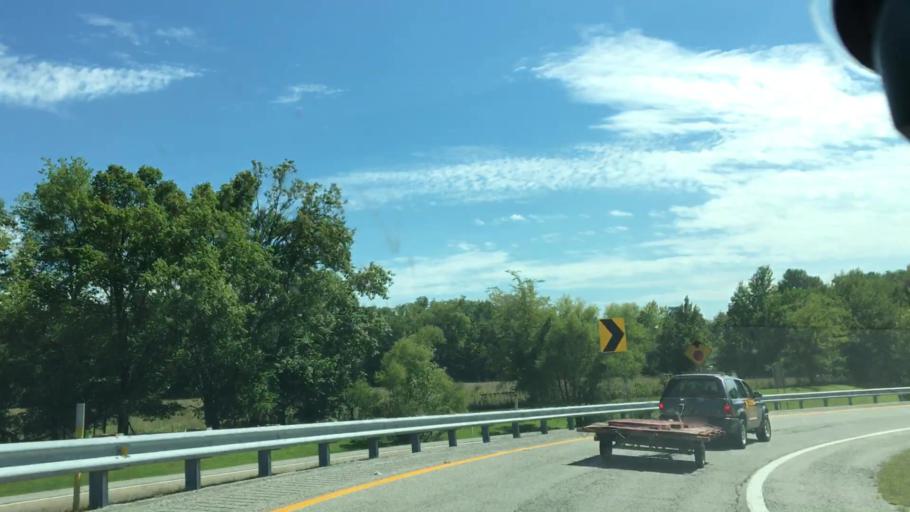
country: US
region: Kentucky
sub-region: Henderson County
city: Henderson
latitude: 37.8317
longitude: -87.5650
